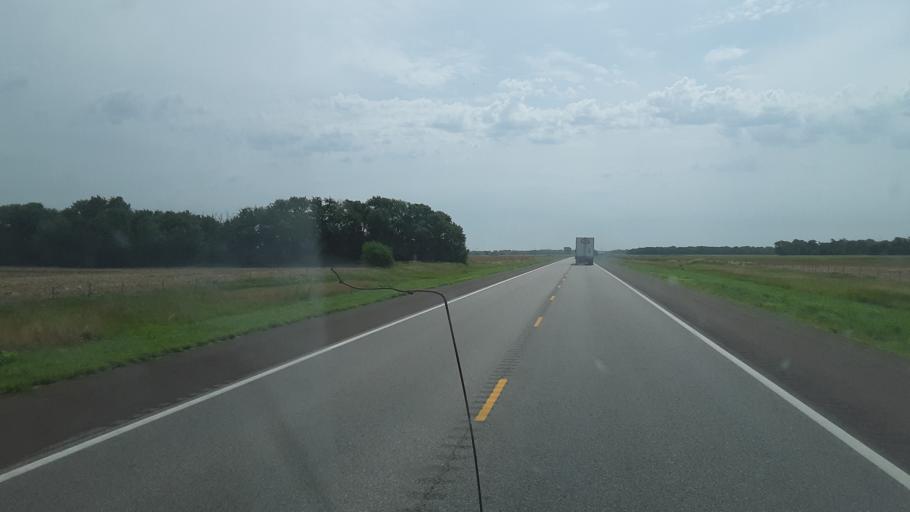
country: US
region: Kansas
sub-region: Reno County
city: Nickerson
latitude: 37.9852
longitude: -98.1697
